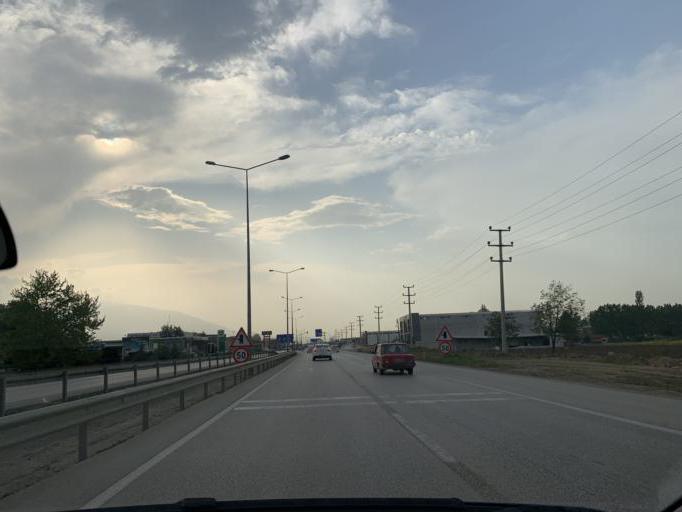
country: TR
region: Bursa
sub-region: Inegoel
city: Inegol
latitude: 40.0740
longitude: 29.5372
